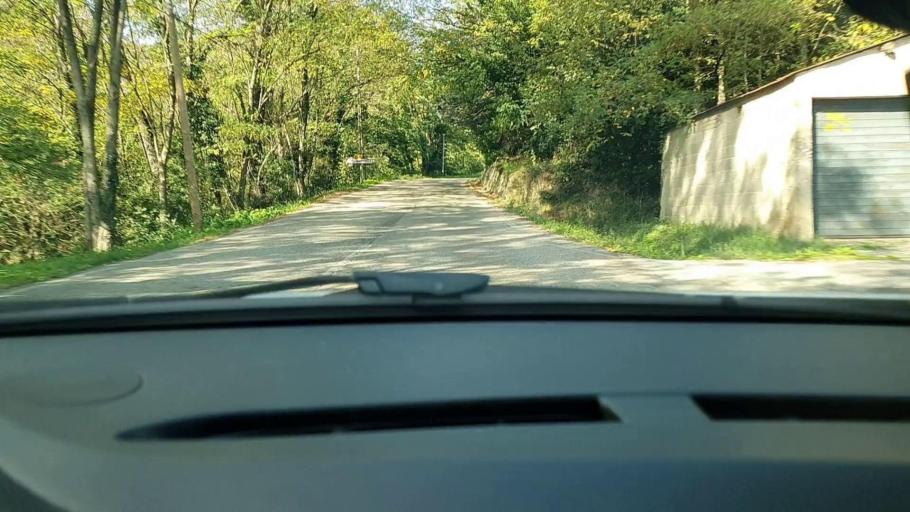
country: FR
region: Languedoc-Roussillon
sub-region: Departement du Gard
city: Besseges
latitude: 44.2783
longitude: 4.0793
